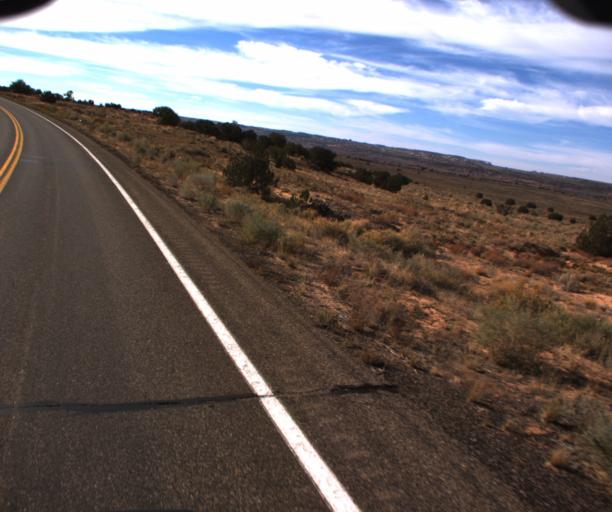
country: US
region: Arizona
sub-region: Coconino County
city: Kaibito
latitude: 36.6730
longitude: -111.2571
